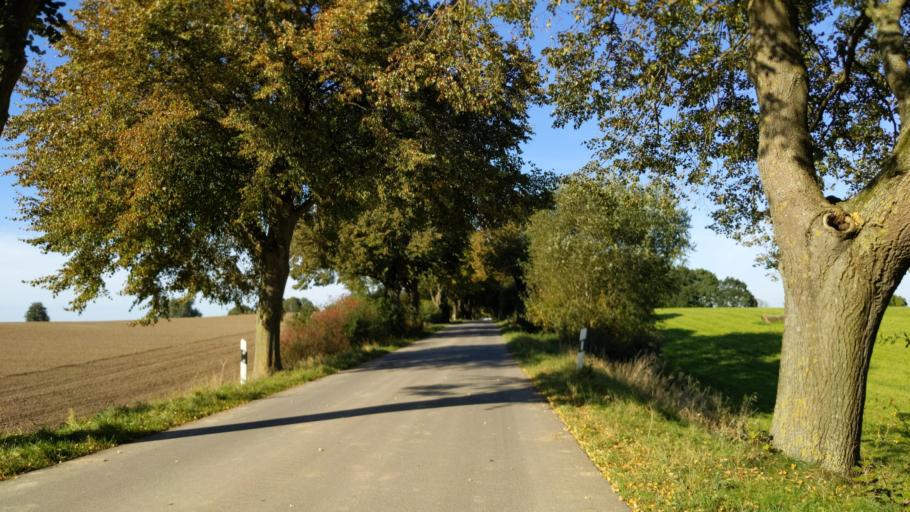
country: DE
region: Schleswig-Holstein
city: Ahrensbok
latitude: 54.0205
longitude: 10.6201
